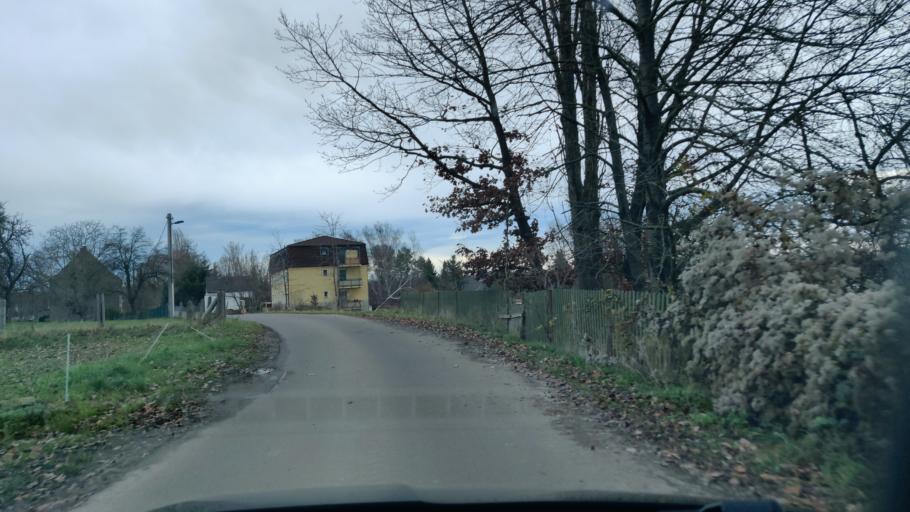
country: DE
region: Saxony
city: Bad Lausick
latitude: 51.1520
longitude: 12.6275
